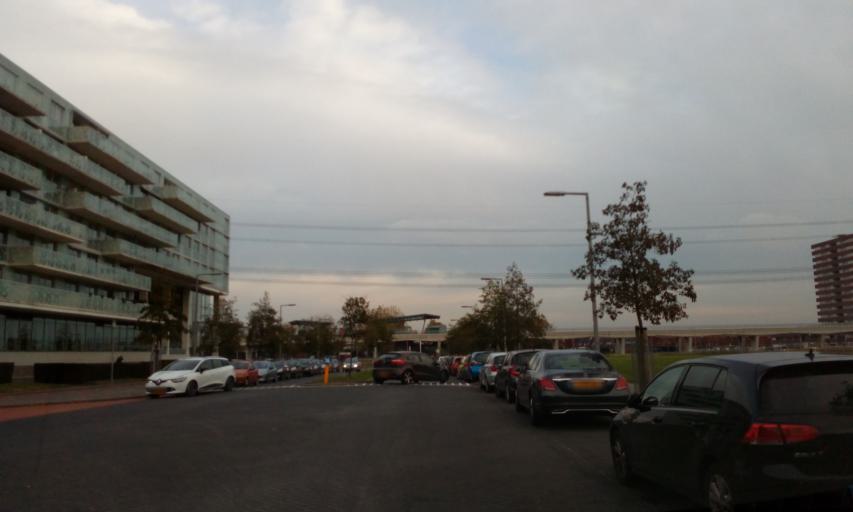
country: NL
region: South Holland
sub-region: Gemeente Capelle aan den IJssel
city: Capelle aan den IJssel
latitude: 51.9796
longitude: 4.5831
